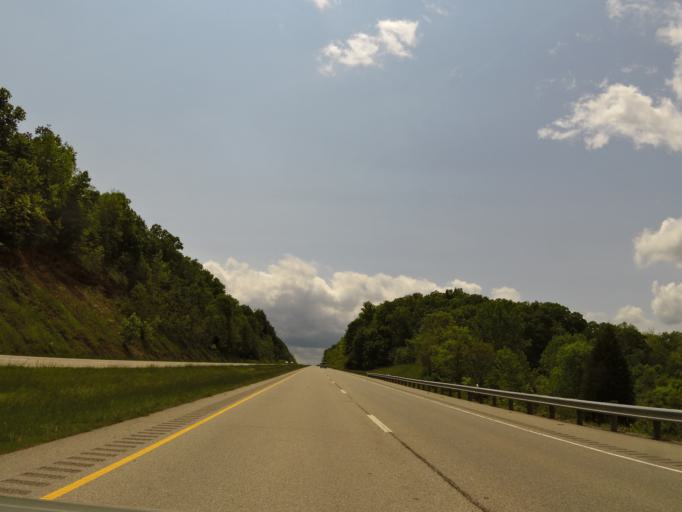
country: US
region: Ohio
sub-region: Meigs County
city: Pomeroy
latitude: 39.0948
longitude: -82.0138
